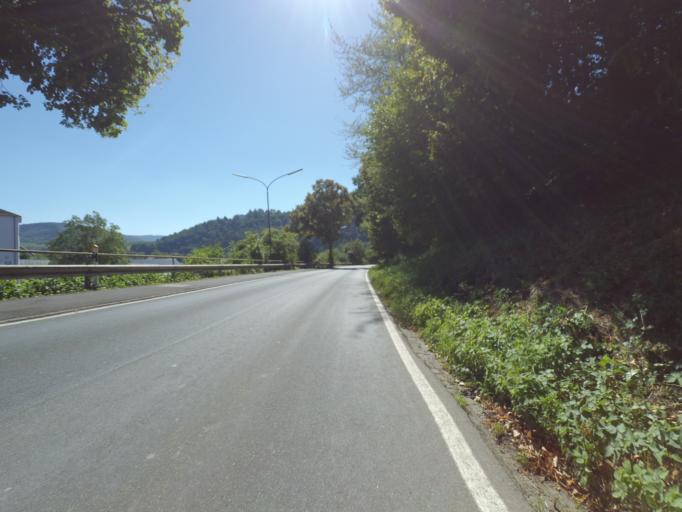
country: DE
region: Rheinland-Pfalz
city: Bullay
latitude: 50.0506
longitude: 7.1355
